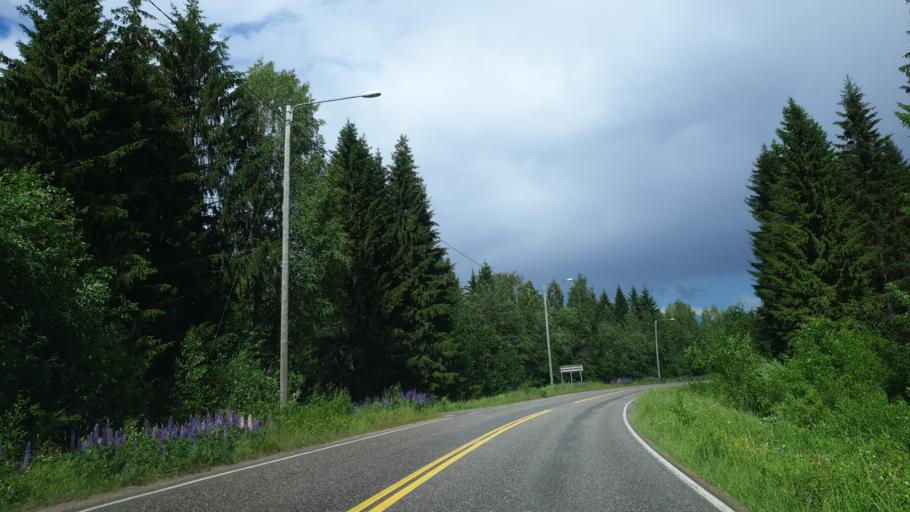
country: FI
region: Northern Savo
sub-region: Kuopio
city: Kuopio
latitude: 62.9061
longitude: 27.8449
